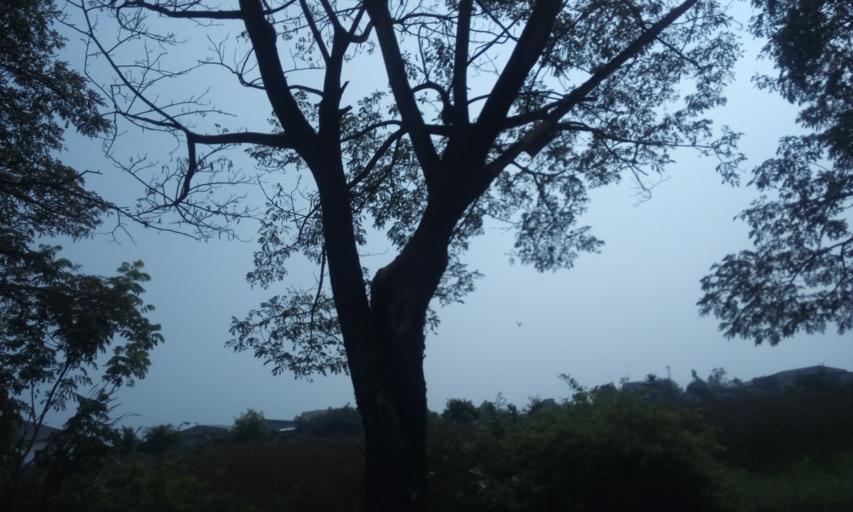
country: TH
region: Pathum Thani
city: Lam Luk Ka
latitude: 13.9646
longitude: 100.7309
